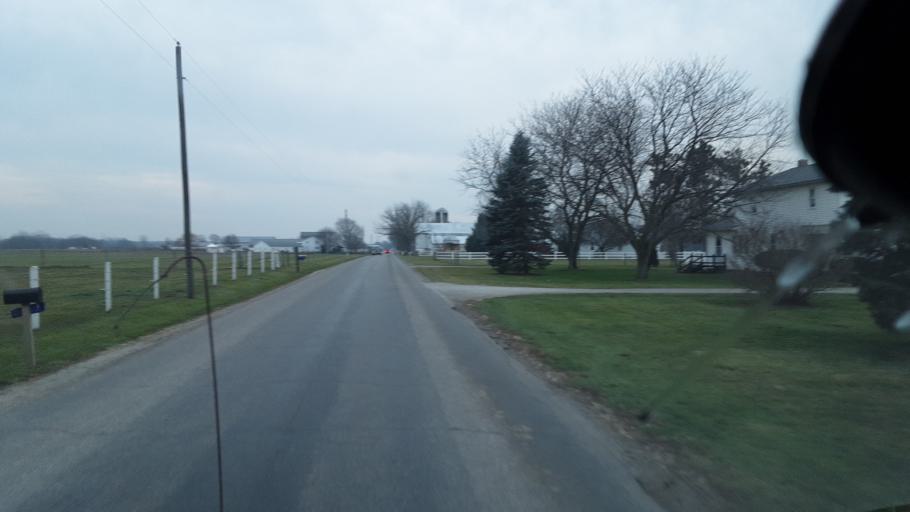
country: US
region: Indiana
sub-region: Elkhart County
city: Middlebury
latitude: 41.6968
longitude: -85.6201
